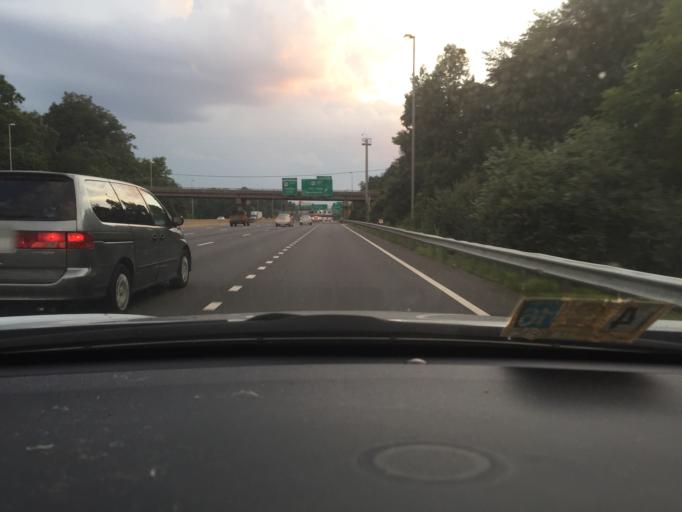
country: US
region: Virginia
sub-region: City of Fairfax
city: Fairfax
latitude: 38.8643
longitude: -77.3348
